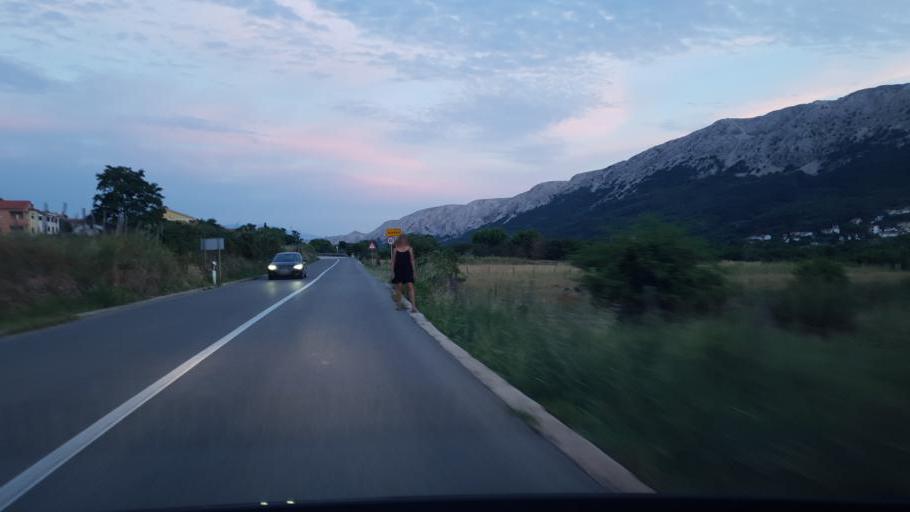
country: HR
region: Primorsko-Goranska
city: Punat
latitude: 44.9816
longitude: 14.7303
